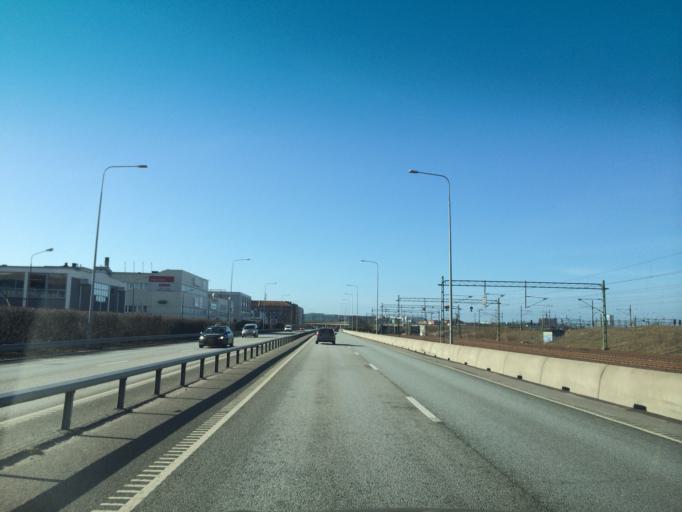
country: SE
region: Skane
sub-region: Malmo
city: Malmoe
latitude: 55.6134
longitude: 13.0369
